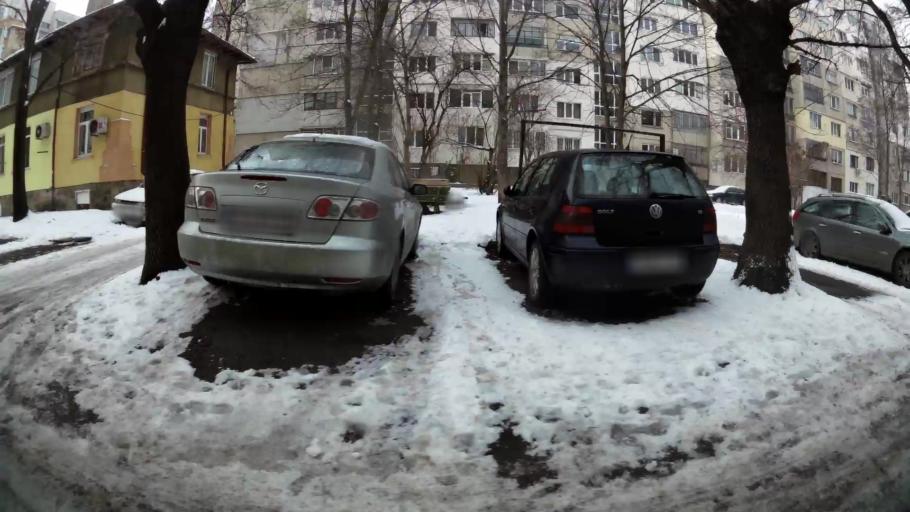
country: BG
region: Sofia-Capital
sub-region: Stolichna Obshtina
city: Sofia
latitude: 42.7133
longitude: 23.3019
